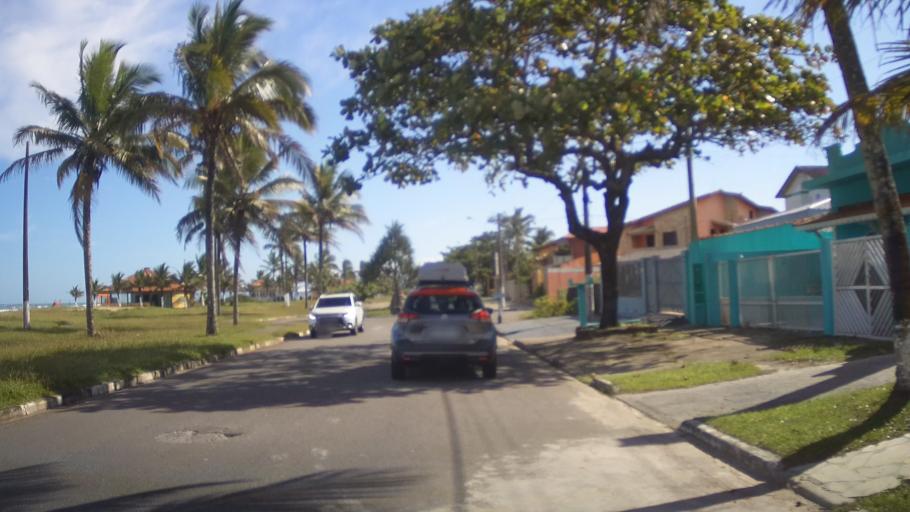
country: BR
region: Sao Paulo
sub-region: Itanhaem
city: Itanhaem
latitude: -24.2036
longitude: -46.8226
